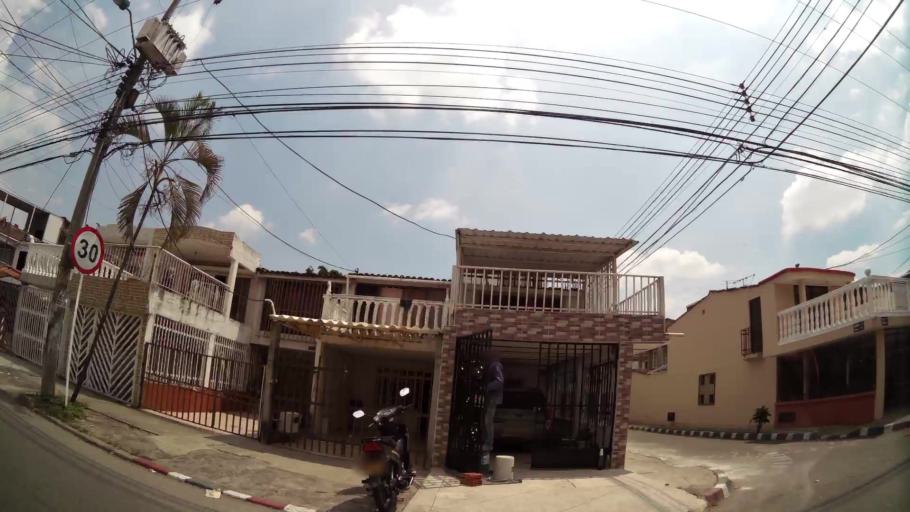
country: CO
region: Valle del Cauca
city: Cali
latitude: 3.4738
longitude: -76.5013
